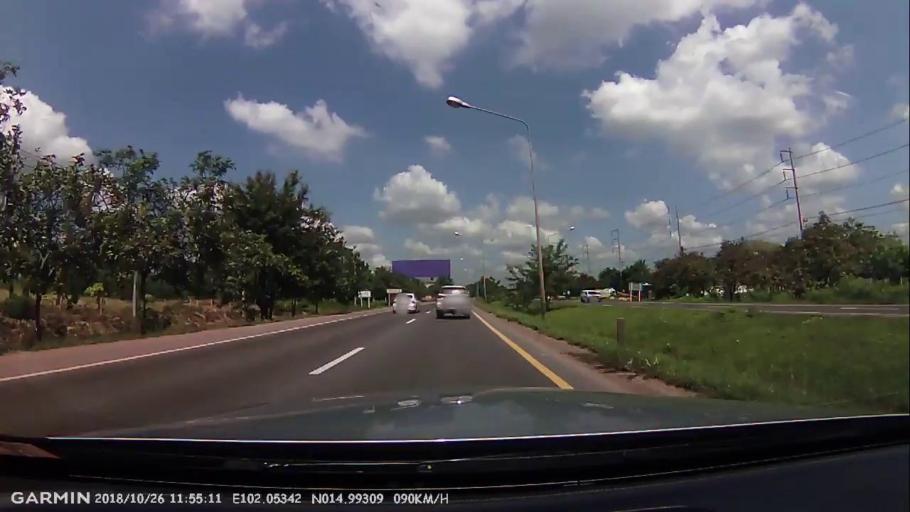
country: TH
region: Nakhon Ratchasima
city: Nakhon Ratchasima
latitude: 14.9933
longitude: 102.0535
